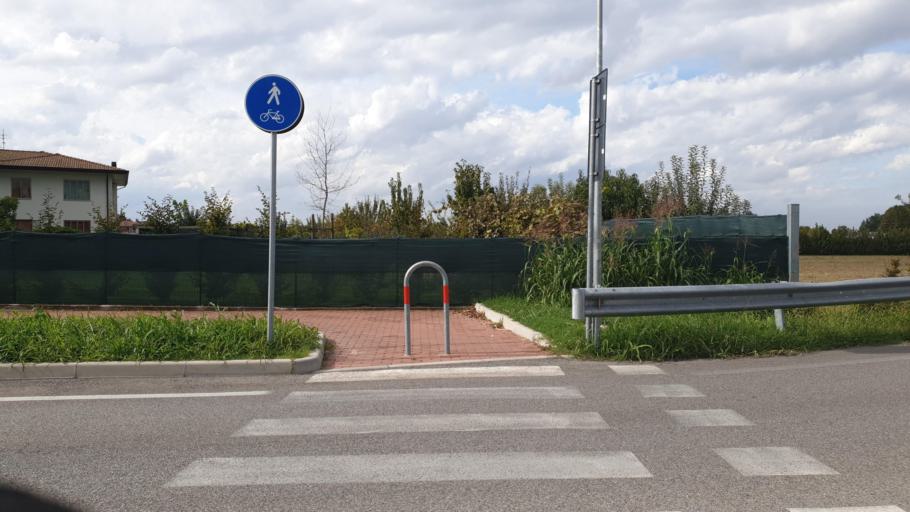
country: IT
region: Veneto
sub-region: Provincia di Padova
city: Campagnola
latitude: 45.2755
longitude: 12.0111
